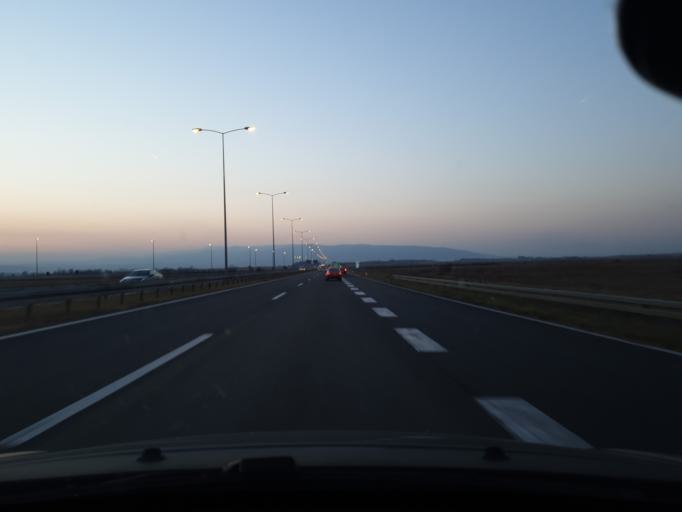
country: RS
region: Central Serbia
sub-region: Nisavski Okrug
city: Nis
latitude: 43.3503
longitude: 21.8512
